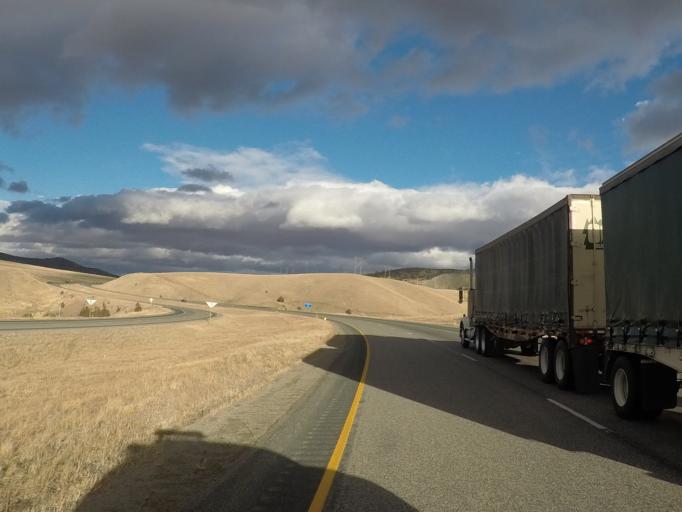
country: US
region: Montana
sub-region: Jefferson County
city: Whitehall
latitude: 45.8793
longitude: -111.8752
